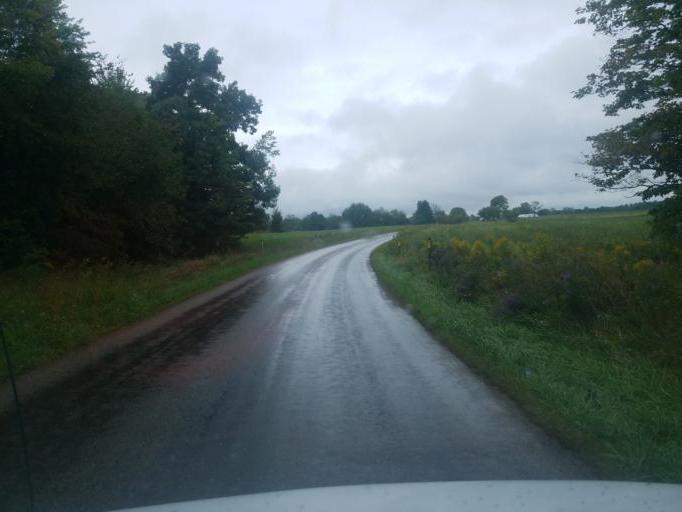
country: US
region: Ohio
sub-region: Wayne County
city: West Salem
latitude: 40.9372
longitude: -82.0909
